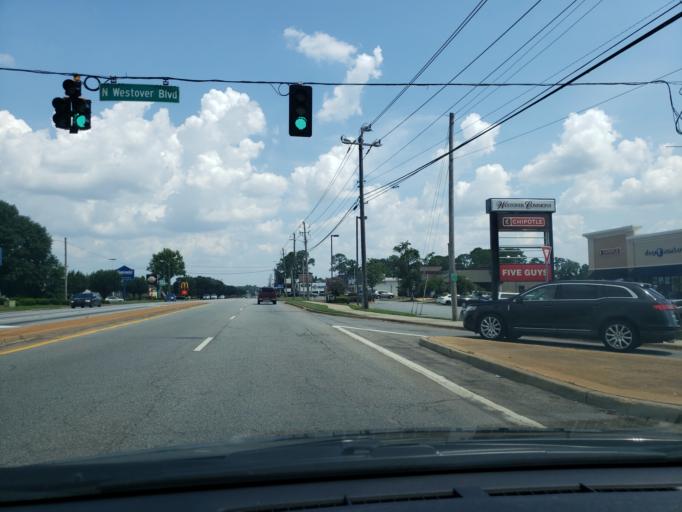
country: US
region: Georgia
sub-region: Dougherty County
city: Albany
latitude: 31.6177
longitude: -84.2222
